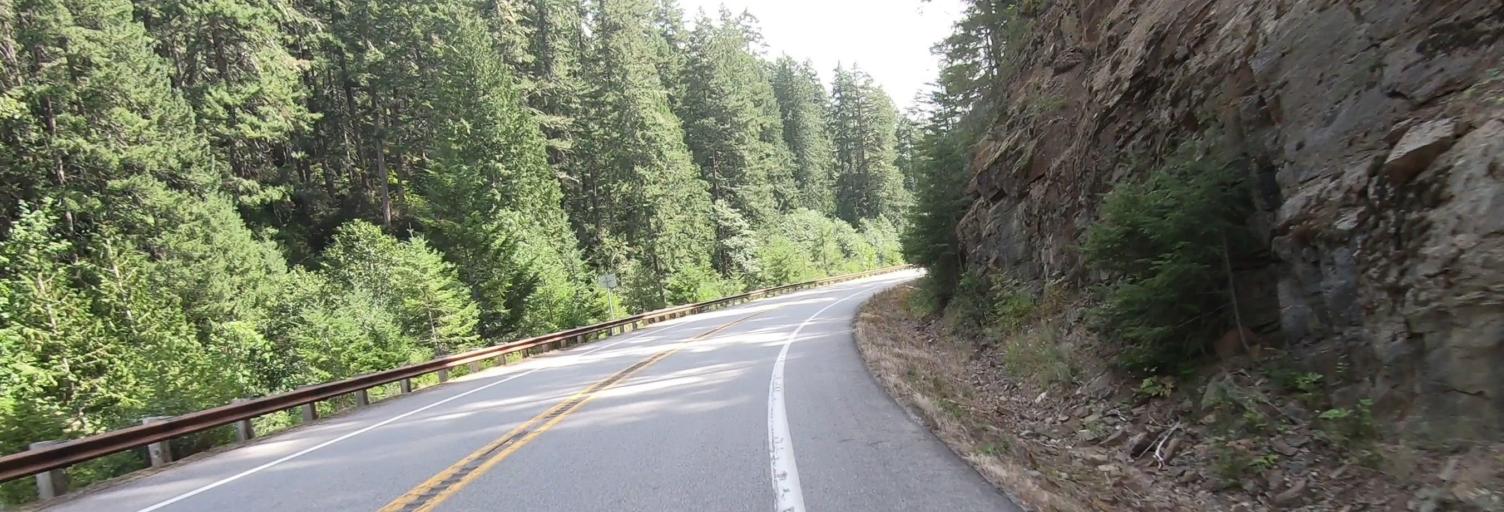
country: US
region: Washington
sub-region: Snohomish County
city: Darrington
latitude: 48.6874
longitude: -120.9125
